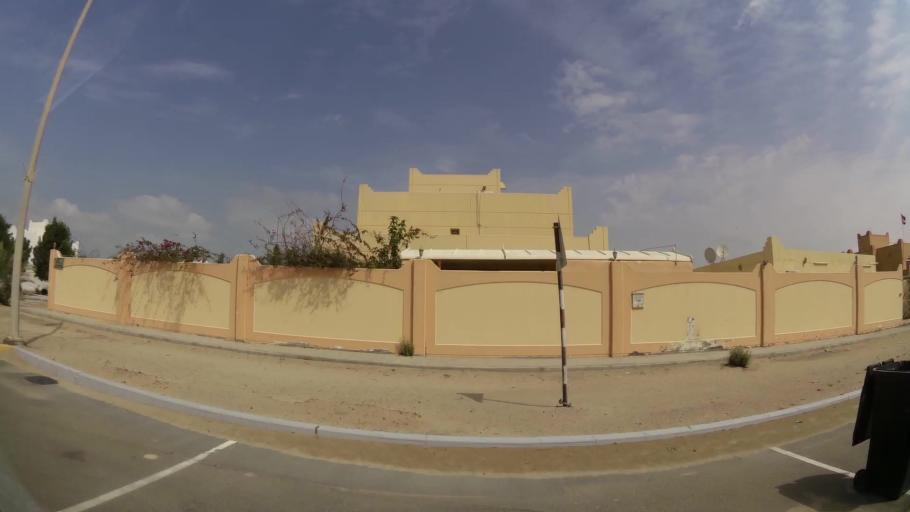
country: AE
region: Abu Dhabi
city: Abu Dhabi
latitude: 24.5534
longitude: 54.6369
